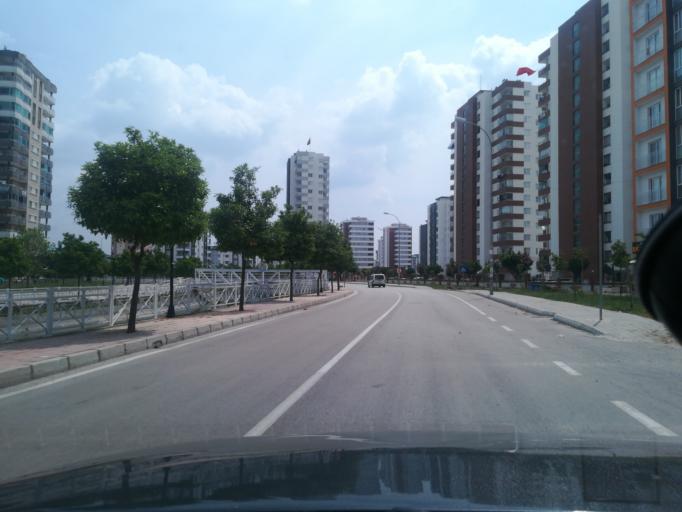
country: TR
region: Adana
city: Seyhan
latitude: 37.0246
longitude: 35.2564
